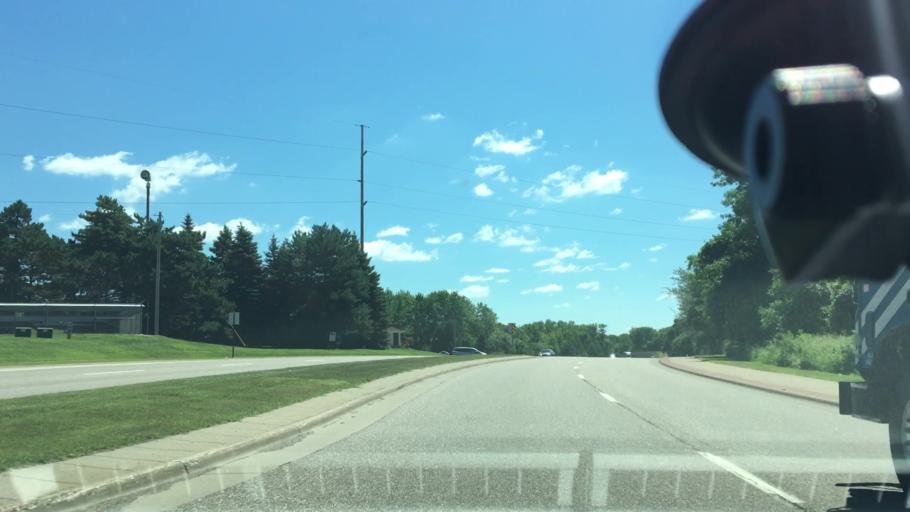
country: US
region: Minnesota
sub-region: Hennepin County
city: Maple Grove
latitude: 45.0759
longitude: -93.4630
